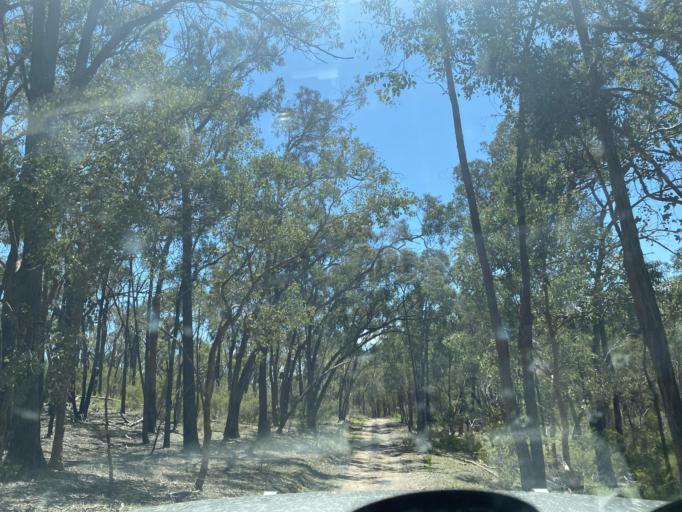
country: AU
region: Victoria
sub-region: Benalla
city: Benalla
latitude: -36.7005
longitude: 146.1518
